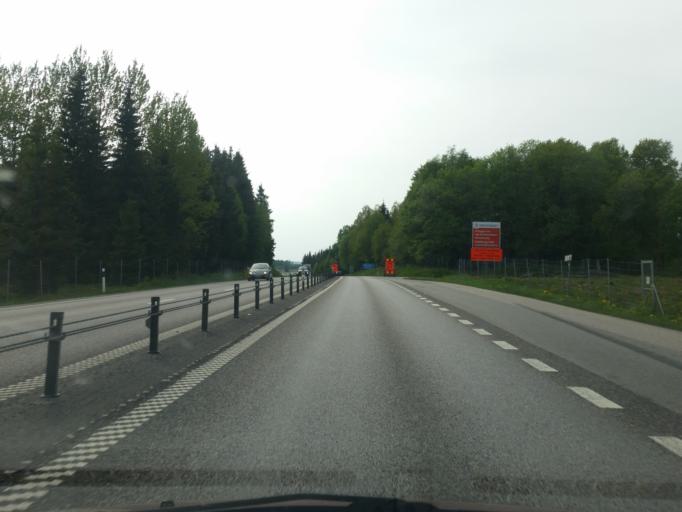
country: SE
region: Vaestra Goetaland
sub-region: Ulricehamns Kommun
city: Ulricehamn
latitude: 57.8022
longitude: 13.4980
